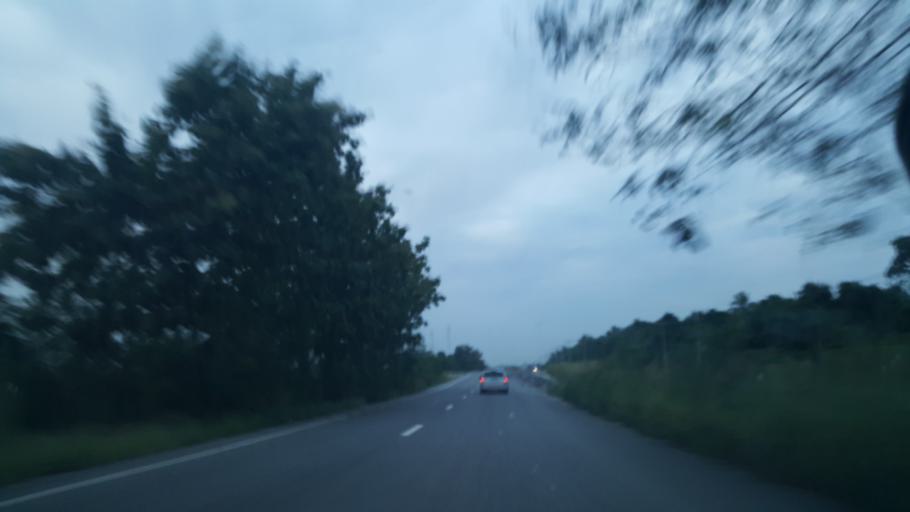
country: TH
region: Rayong
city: Ban Chang
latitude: 12.8487
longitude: 101.0162
